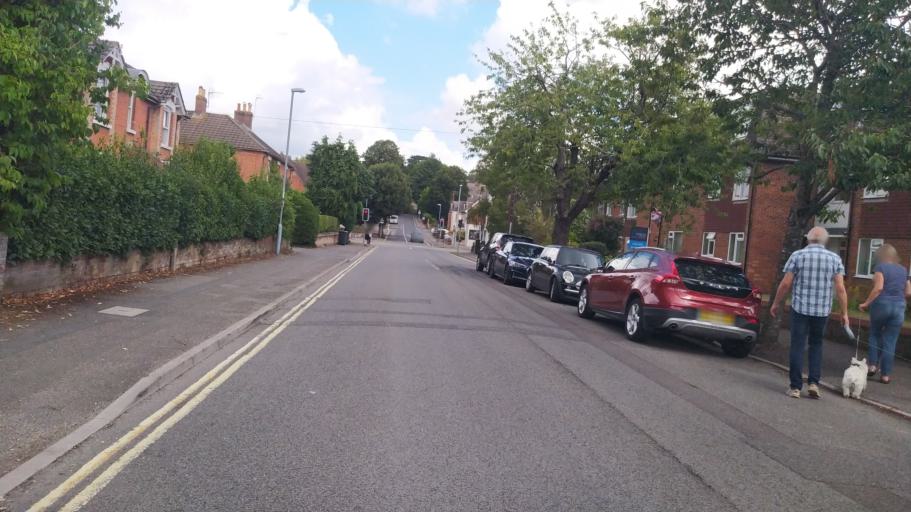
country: GB
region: England
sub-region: Dorset
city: Wimborne Minster
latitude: 50.7971
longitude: -1.9780
